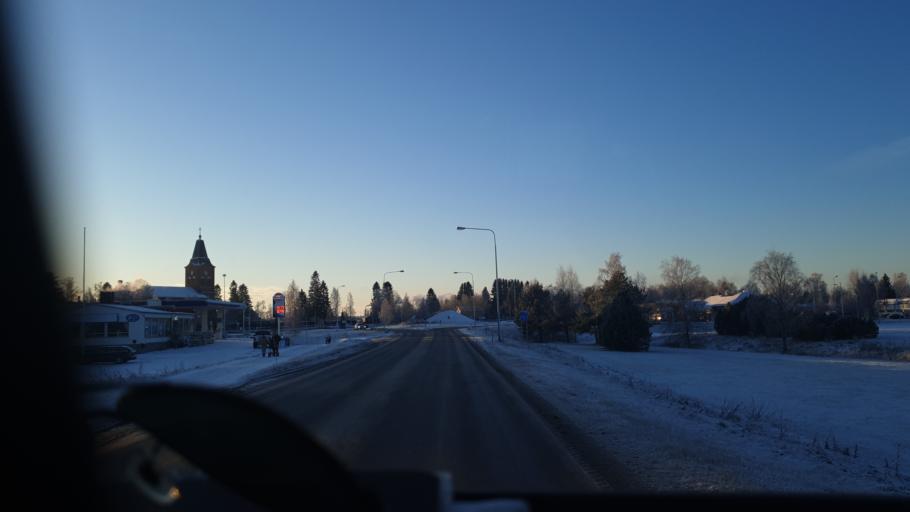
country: FI
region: Northern Ostrobothnia
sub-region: Ylivieska
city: Kalajoki
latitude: 64.2569
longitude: 23.9396
